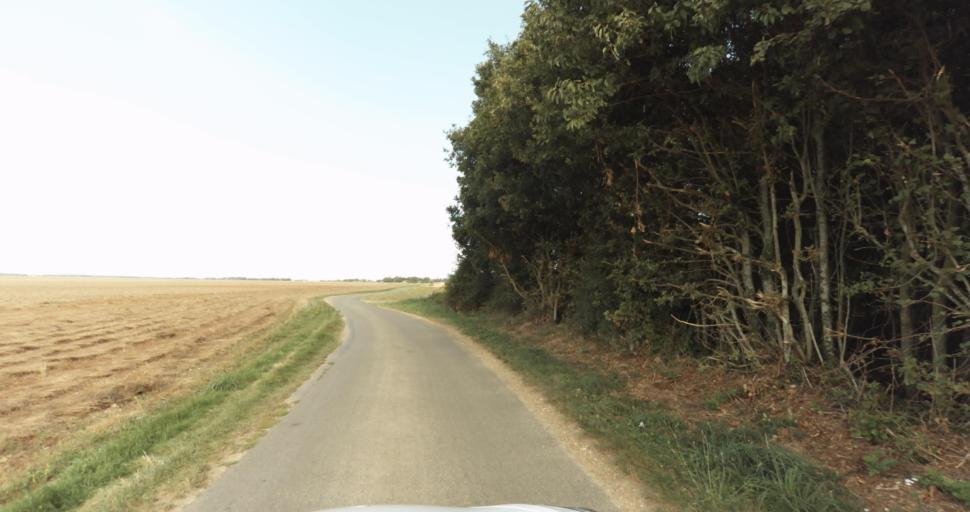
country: FR
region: Haute-Normandie
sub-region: Departement de l'Eure
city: Nonancourt
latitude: 48.8217
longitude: 1.1613
